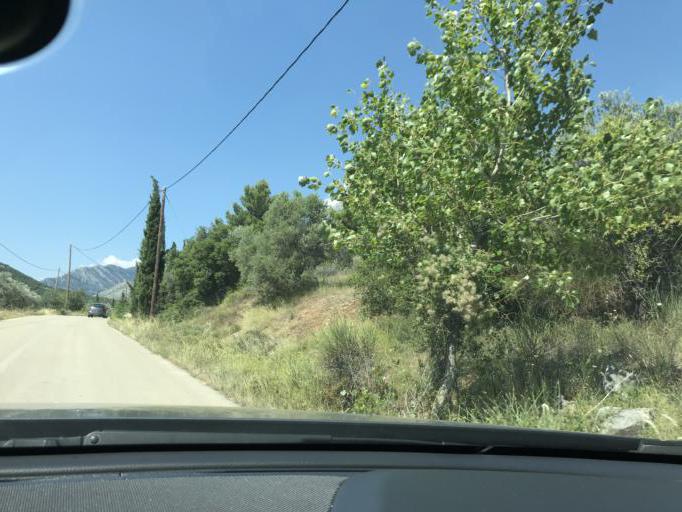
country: GR
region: Central Greece
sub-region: Nomos Voiotias
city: Distomo
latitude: 38.5111
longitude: 22.7197
